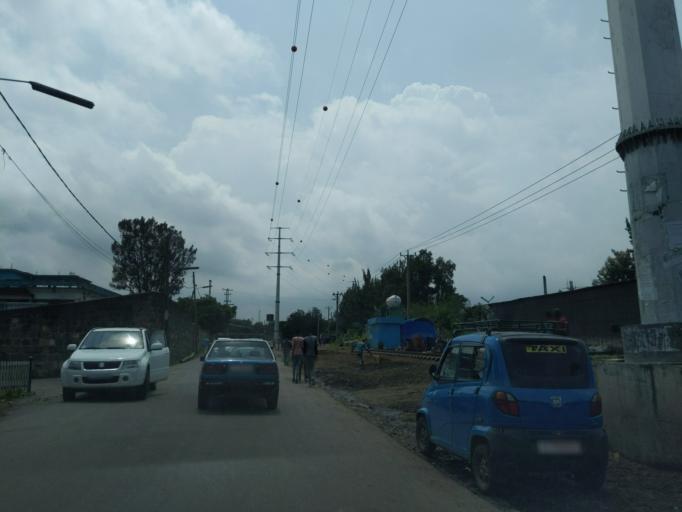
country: ET
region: Adis Abeba
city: Addis Ababa
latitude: 8.9551
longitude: 38.7611
